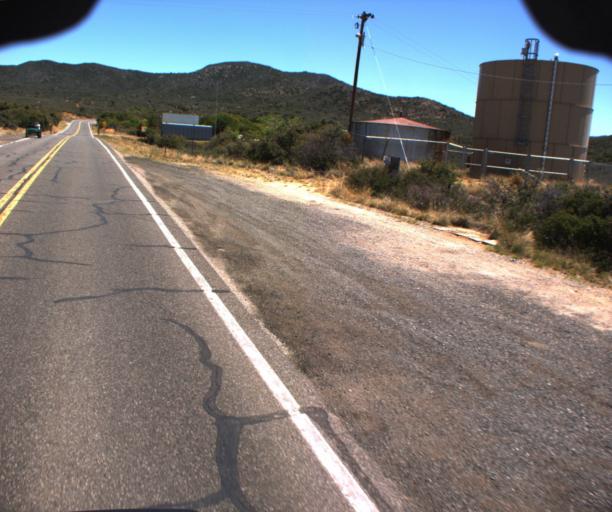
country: US
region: Arizona
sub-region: Yavapai County
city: Prescott
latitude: 34.4259
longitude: -112.5865
